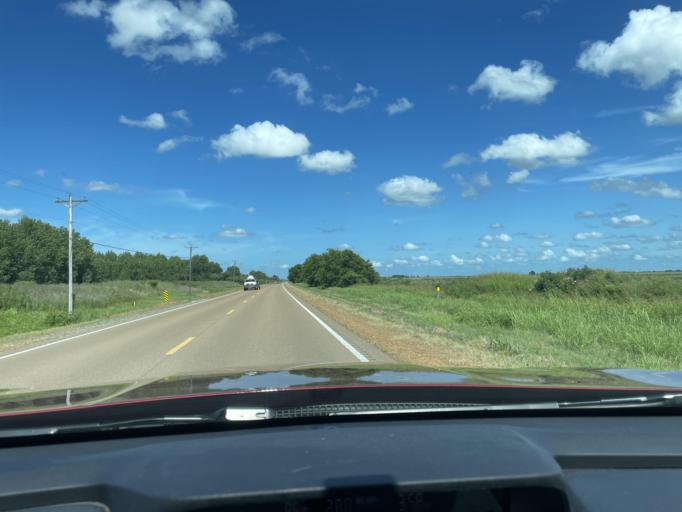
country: US
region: Mississippi
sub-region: Humphreys County
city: Belzoni
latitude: 33.1836
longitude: -90.5927
